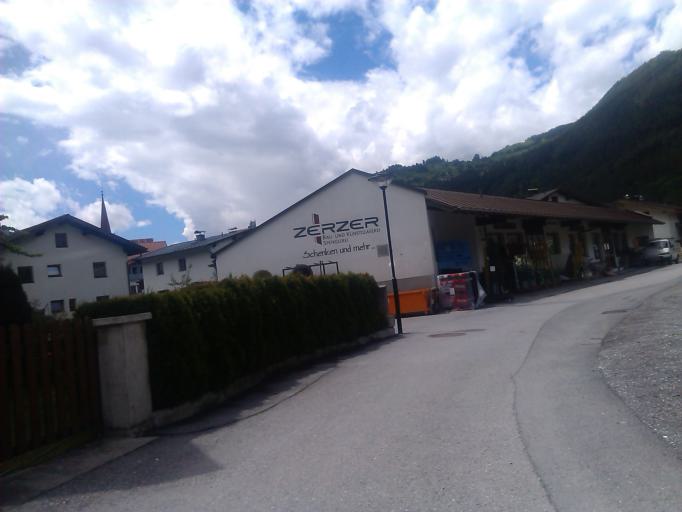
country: AT
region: Tyrol
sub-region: Politischer Bezirk Landeck
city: Ried im Oberinntal
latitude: 47.0562
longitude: 10.6555
